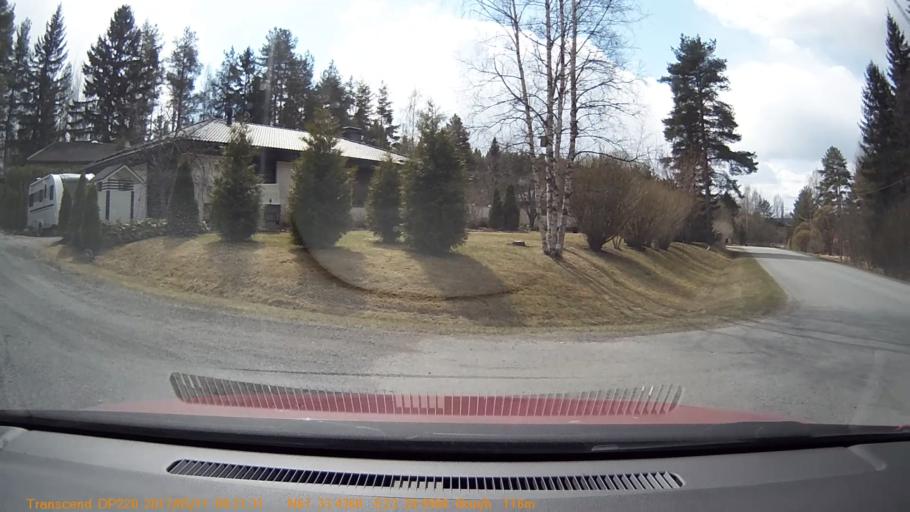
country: FI
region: Pirkanmaa
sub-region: Tampere
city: Yloejaervi
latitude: 61.5572
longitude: 23.6669
